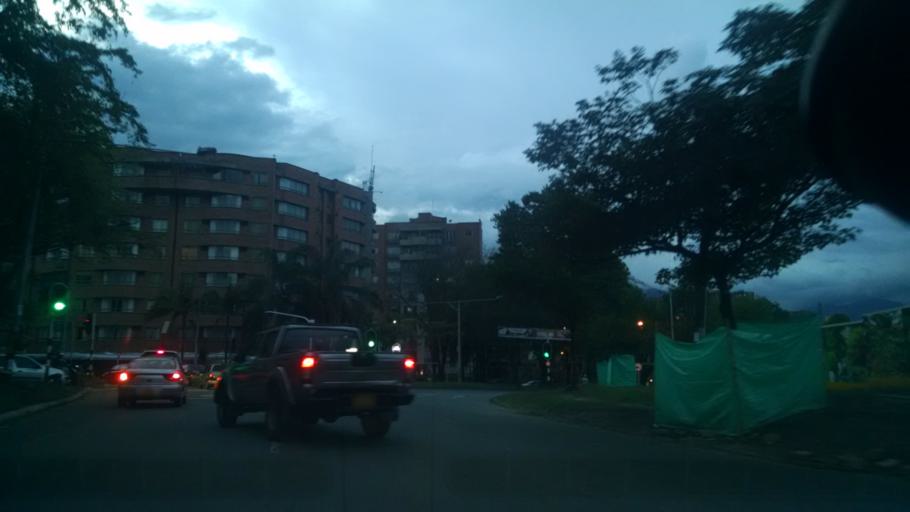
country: CO
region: Antioquia
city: Itagui
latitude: 6.2109
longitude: -75.5946
